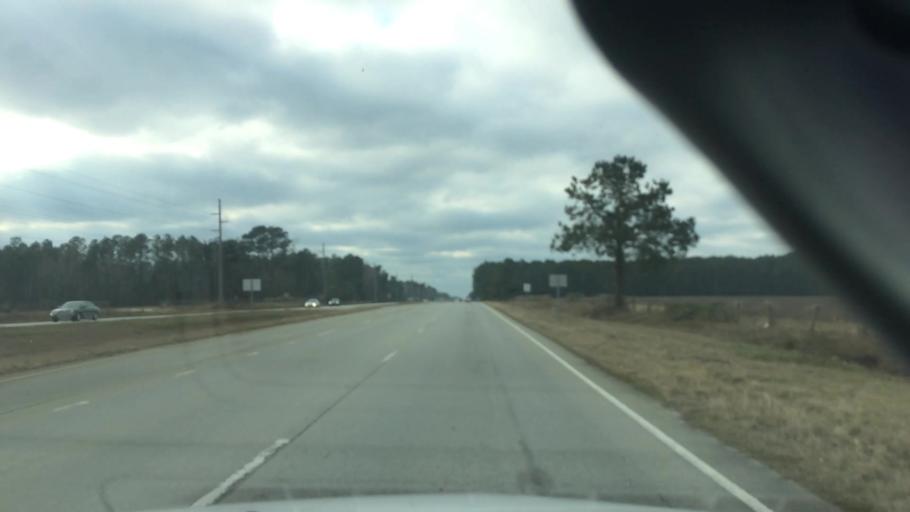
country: US
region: North Carolina
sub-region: Brunswick County
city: Shallotte
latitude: 33.9562
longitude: -78.4391
